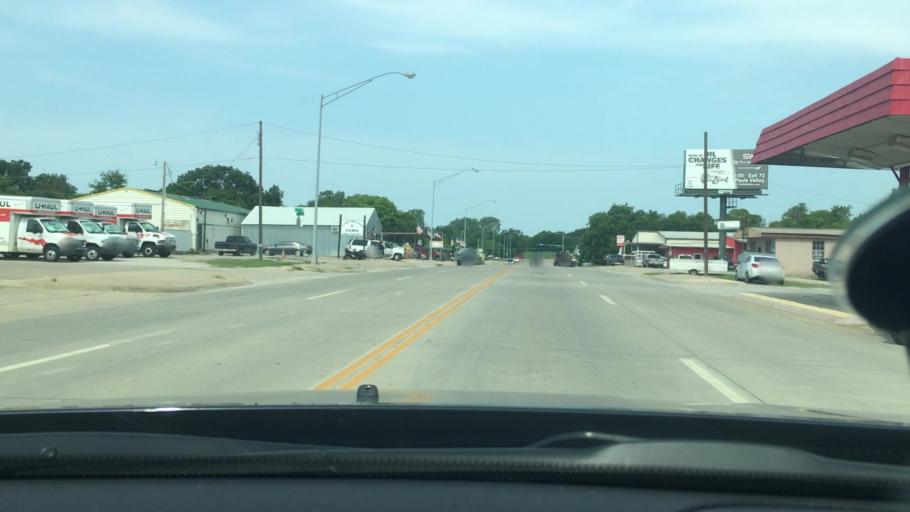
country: US
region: Oklahoma
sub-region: Carter County
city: Ardmore
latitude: 34.1856
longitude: -97.1186
